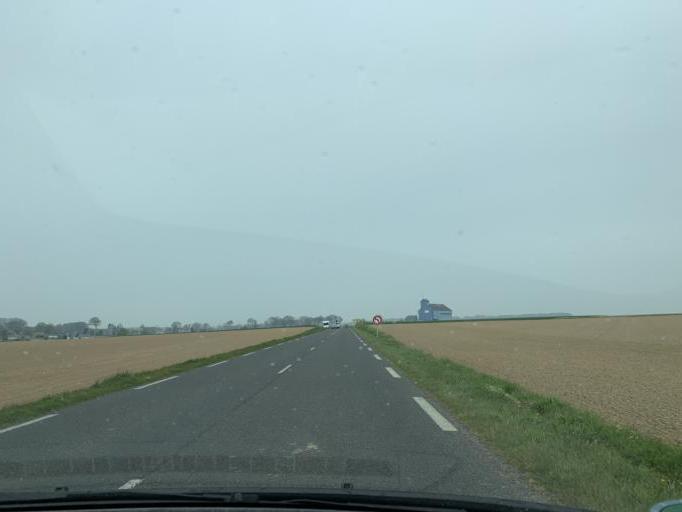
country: FR
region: Haute-Normandie
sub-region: Departement de la Seine-Maritime
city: Neville
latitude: 49.8139
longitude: 0.6700
